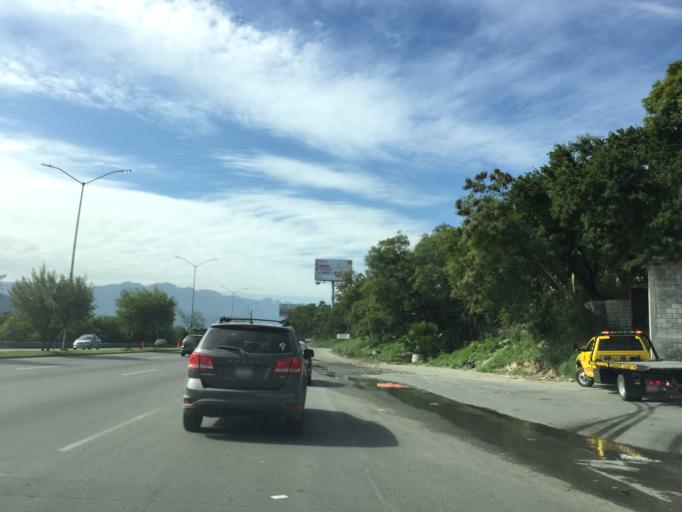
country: MX
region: Nuevo Leon
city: Guadalupe
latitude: 25.6933
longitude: -100.2141
